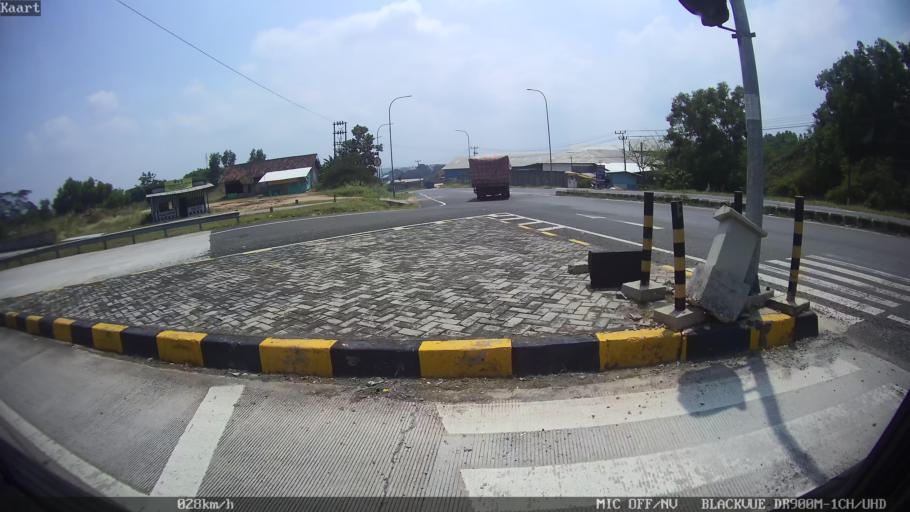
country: ID
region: Lampung
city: Panjang
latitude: -5.4080
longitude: 105.3483
